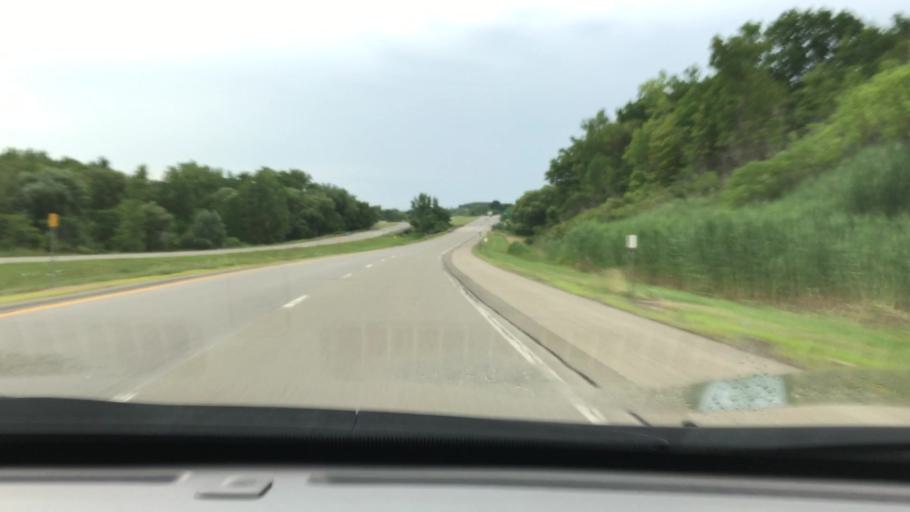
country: US
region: New York
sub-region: Erie County
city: North Boston
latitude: 42.6880
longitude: -78.7875
